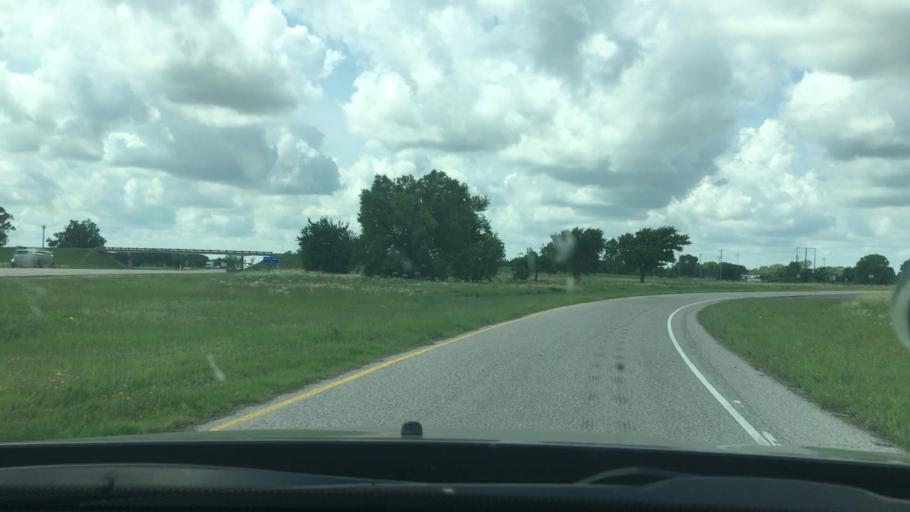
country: US
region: Oklahoma
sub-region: Love County
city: Marietta
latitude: 33.7980
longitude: -97.1352
